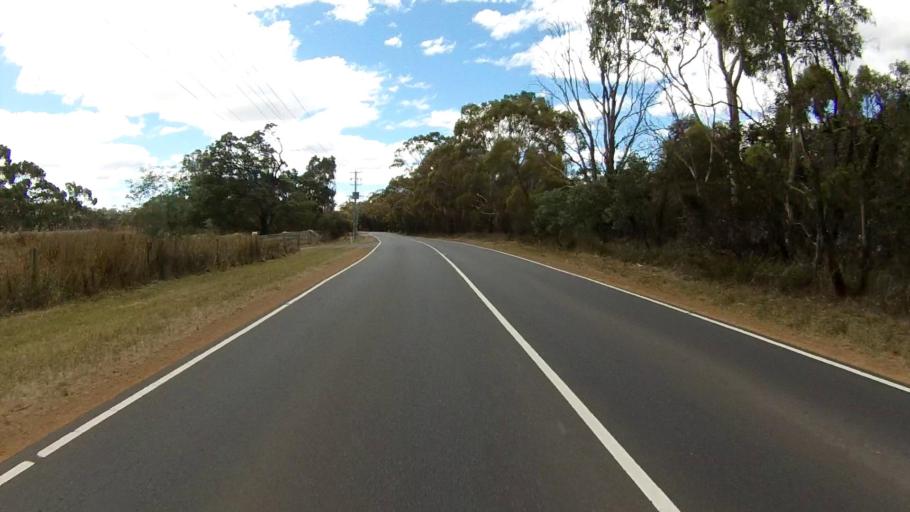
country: AU
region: Tasmania
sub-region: Clarence
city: Acton Park
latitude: -42.8769
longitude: 147.4826
